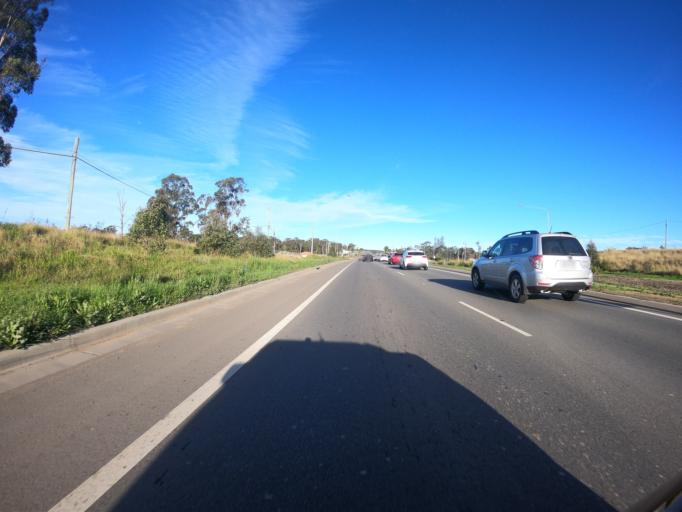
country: AU
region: New South Wales
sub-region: Blacktown
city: Hassall Grove
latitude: -33.6987
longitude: 150.8328
